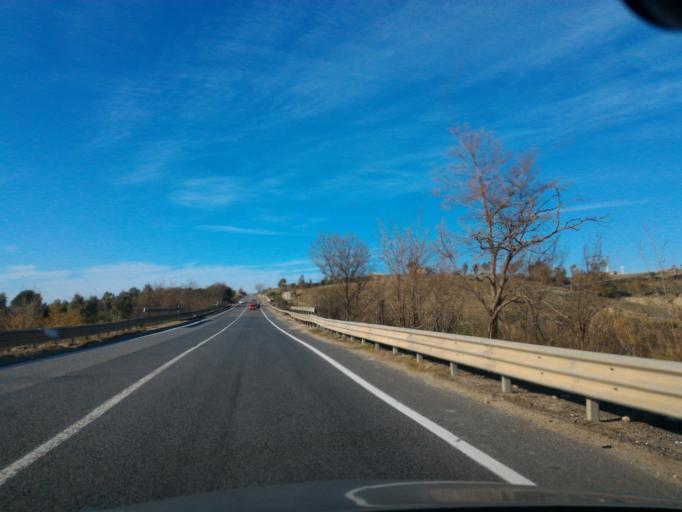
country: IT
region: Calabria
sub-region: Provincia di Crotone
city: Isola di Capo Rizzuto
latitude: 38.9395
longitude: 17.0732
